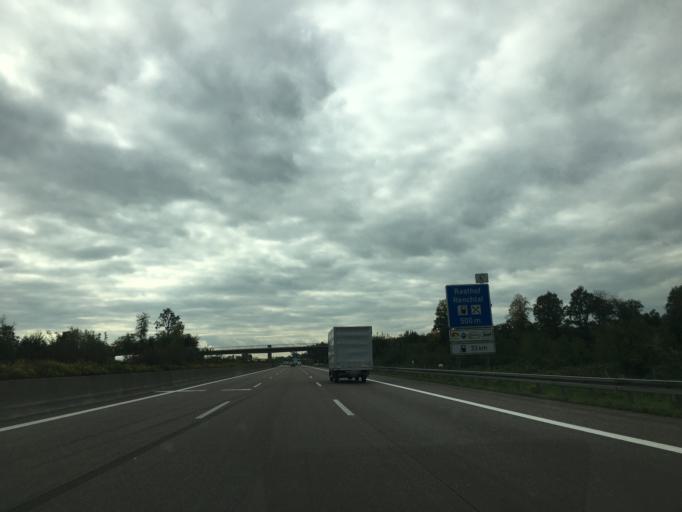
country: DE
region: Baden-Wuerttemberg
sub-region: Freiburg Region
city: Appenweier
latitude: 48.5711
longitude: 7.9621
